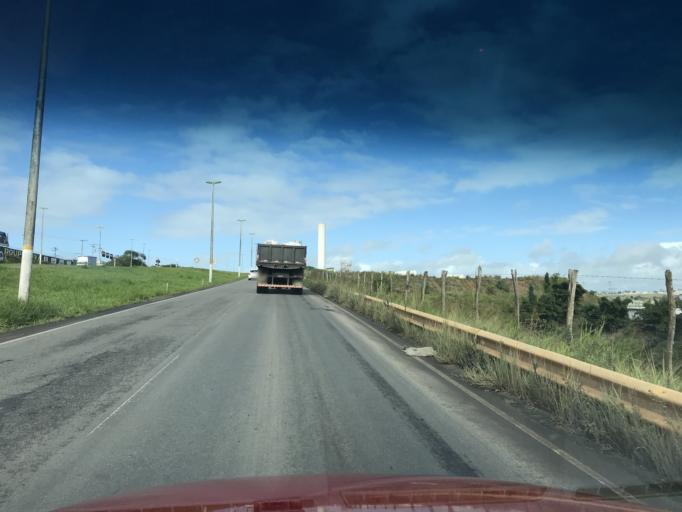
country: BR
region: Bahia
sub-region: Santo Antonio De Jesus
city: Santo Antonio de Jesus
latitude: -12.9624
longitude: -39.2715
